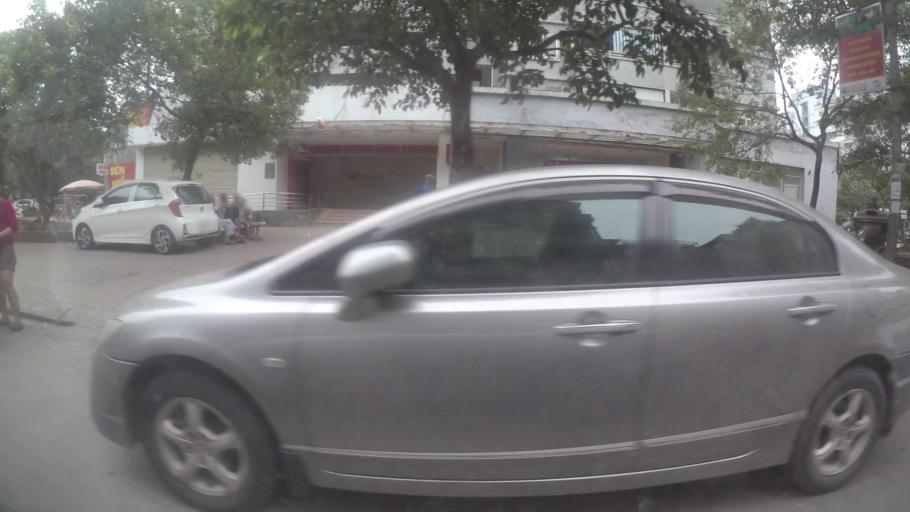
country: VN
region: Ha Noi
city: Cau Dien
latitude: 21.0356
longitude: 105.7640
